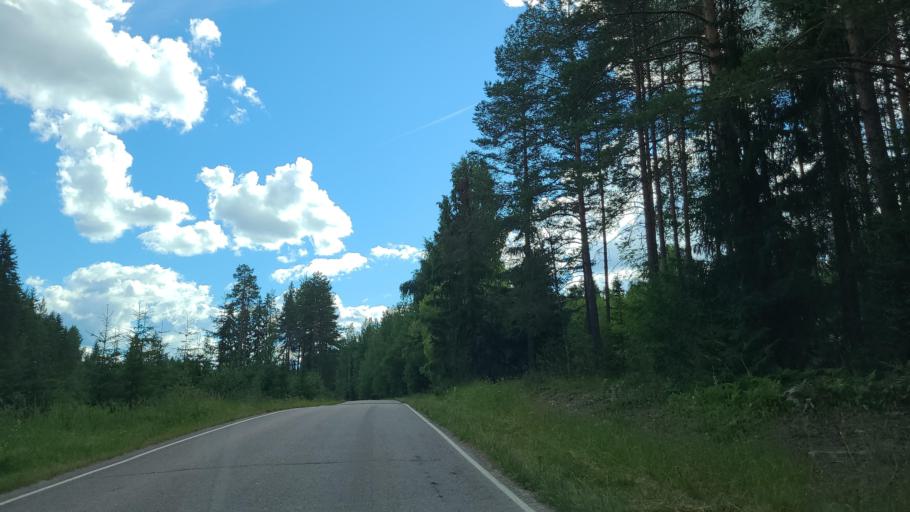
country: FI
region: Central Finland
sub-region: Jaemsae
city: Jaemsae
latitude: 61.8900
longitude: 25.2509
